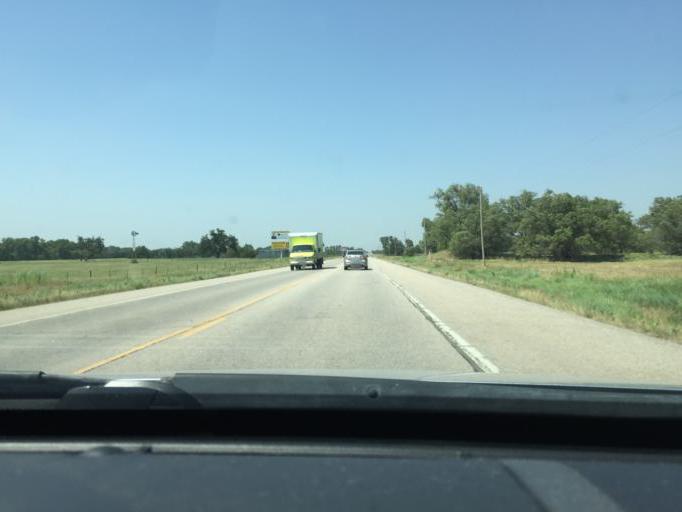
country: US
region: Kansas
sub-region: Reno County
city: South Hutchinson
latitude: 37.9877
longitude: -97.8668
